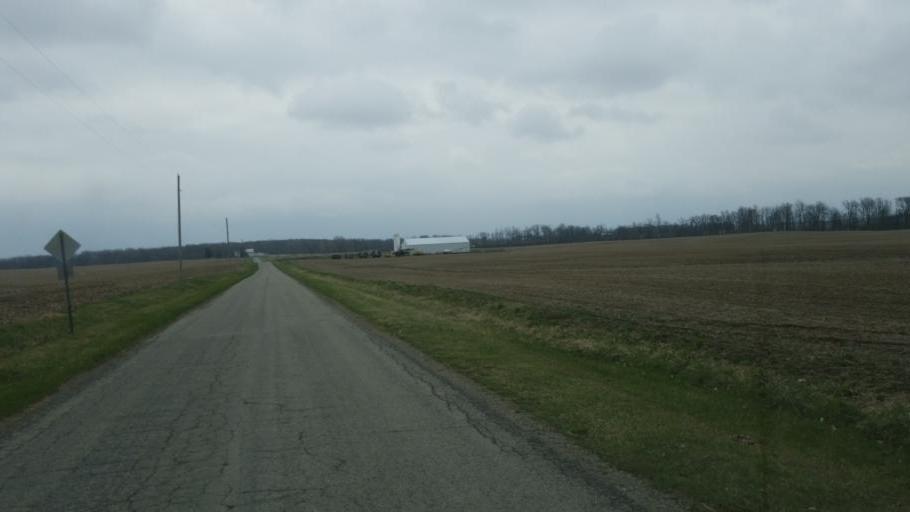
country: US
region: Ohio
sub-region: Union County
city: Richwood
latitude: 40.4181
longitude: -83.3646
